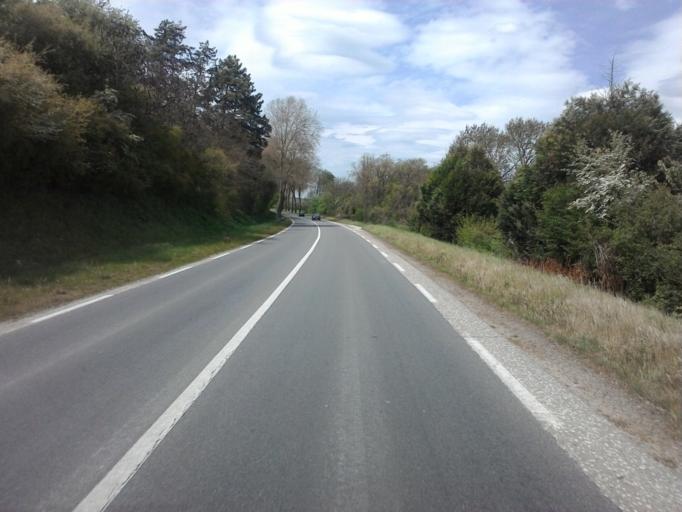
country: FR
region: Bourgogne
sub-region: Departement de l'Yonne
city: Champs-sur-Yonne
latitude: 47.7098
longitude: 3.6246
